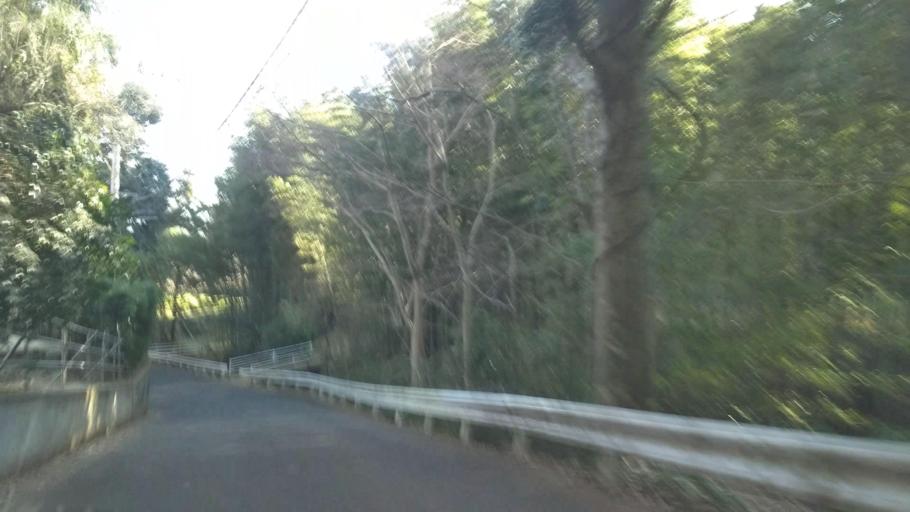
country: JP
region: Kanagawa
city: Hadano
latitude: 35.3714
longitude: 139.2495
